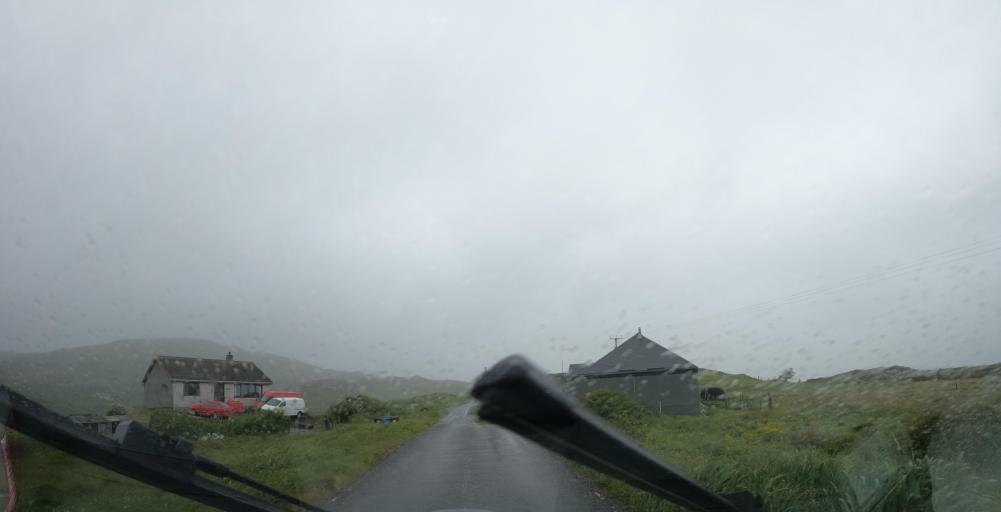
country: GB
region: Scotland
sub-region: Eilean Siar
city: Barra
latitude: 57.0114
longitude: -7.4258
